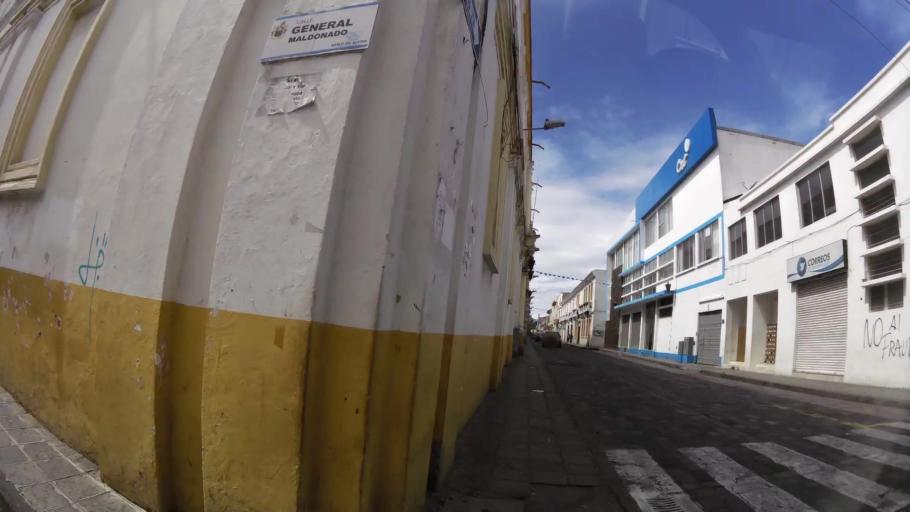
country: EC
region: Cotopaxi
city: Latacunga
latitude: -0.9345
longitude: -78.6160
